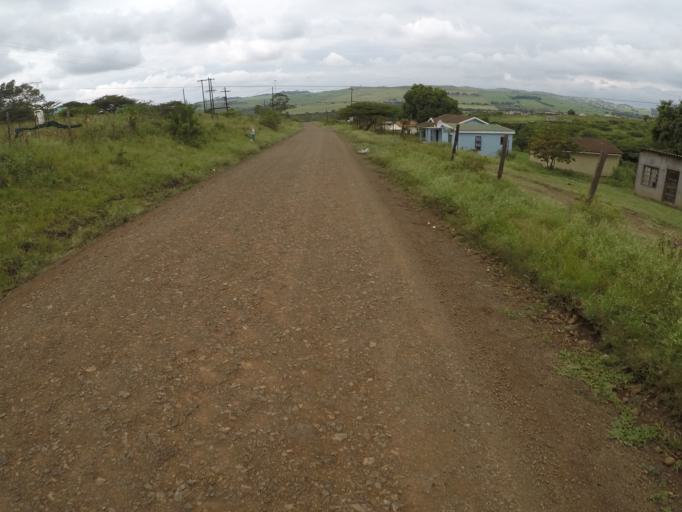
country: ZA
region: KwaZulu-Natal
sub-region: uThungulu District Municipality
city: Empangeni
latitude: -28.7064
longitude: 31.8482
